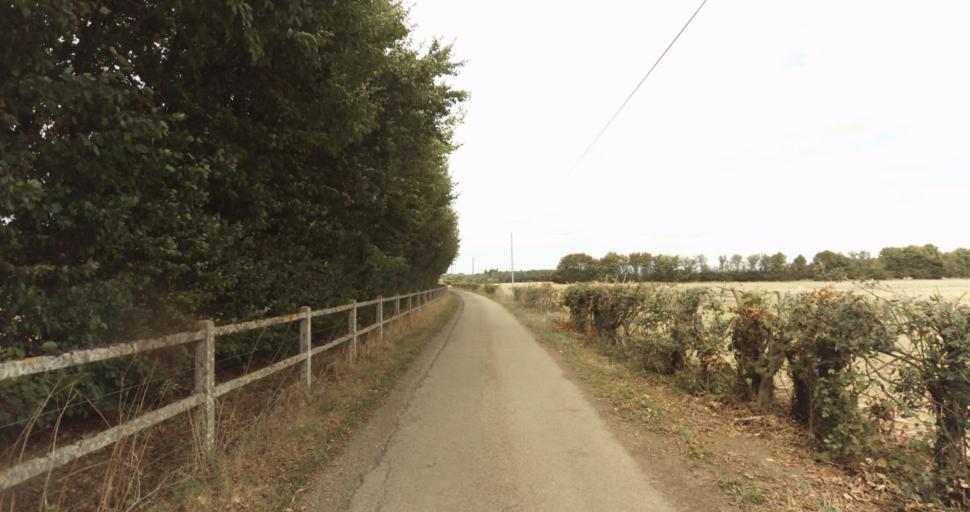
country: FR
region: Lower Normandy
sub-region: Departement de l'Orne
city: Gace
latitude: 48.8891
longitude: 0.3631
